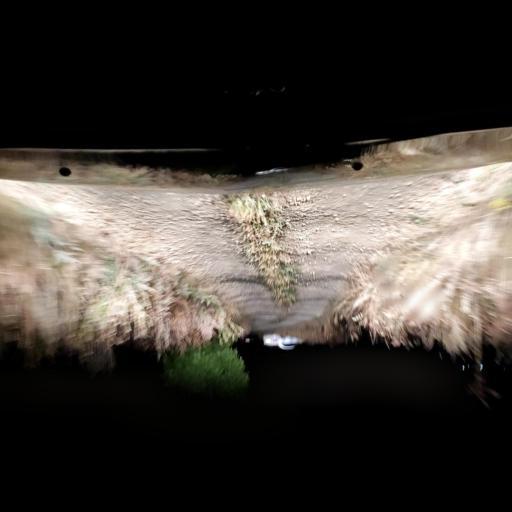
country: RU
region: Voronezj
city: Semiluki
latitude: 51.7182
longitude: 38.9953
